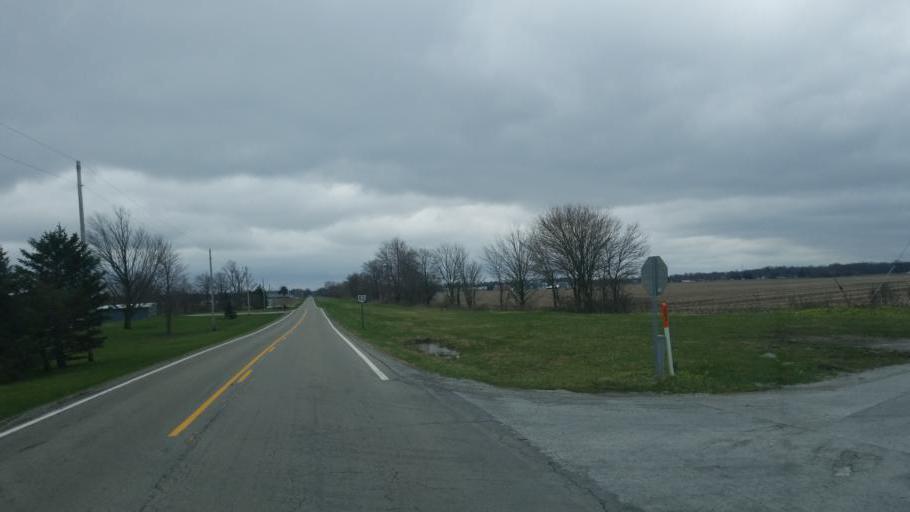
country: US
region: Ohio
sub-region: Hardin County
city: Kenton
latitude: 40.6744
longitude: -83.5956
